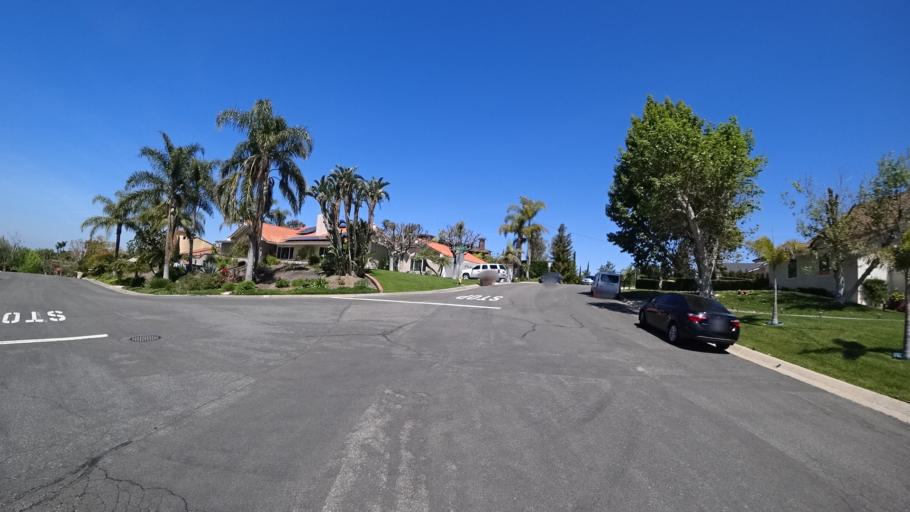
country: US
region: California
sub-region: Orange County
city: Villa Park
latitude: 33.8213
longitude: -117.7976
